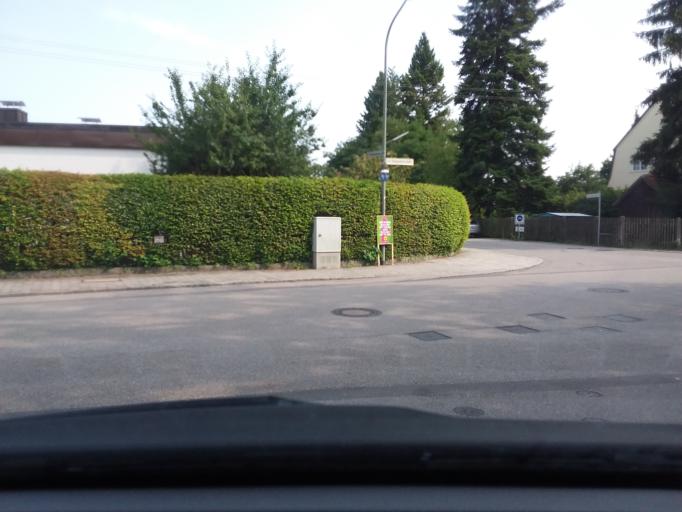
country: DE
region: Bavaria
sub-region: Upper Bavaria
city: Oberschleissheim
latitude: 48.2534
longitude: 11.5480
